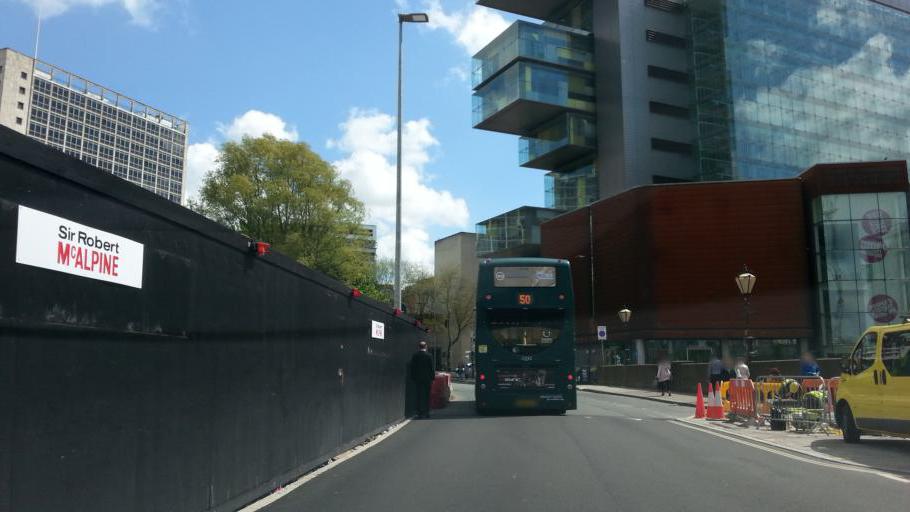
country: GB
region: England
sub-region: Manchester
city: Manchester
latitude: 53.4818
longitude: -2.2537
